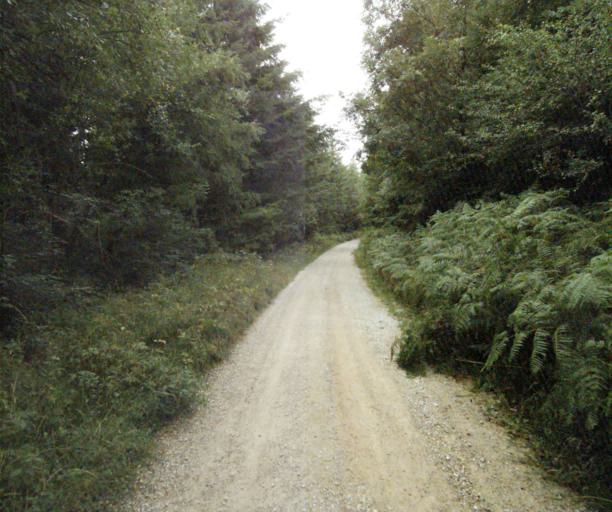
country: FR
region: Midi-Pyrenees
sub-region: Departement du Tarn
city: Soreze
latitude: 43.4311
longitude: 2.1186
